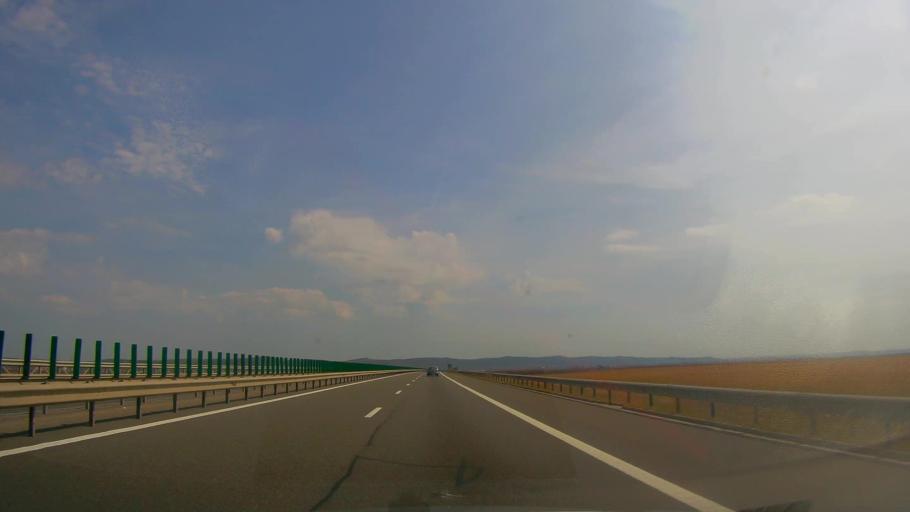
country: RO
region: Cluj
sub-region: Municipiul Campia Turzii
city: Campia Turzii
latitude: 46.5264
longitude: 23.8519
